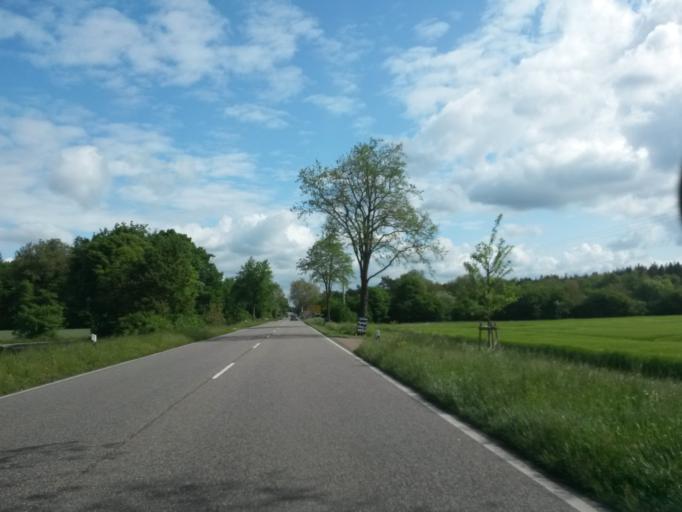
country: DE
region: Baden-Wuerttemberg
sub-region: Karlsruhe Region
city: Graben-Neudorf
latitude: 49.1882
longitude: 8.5052
